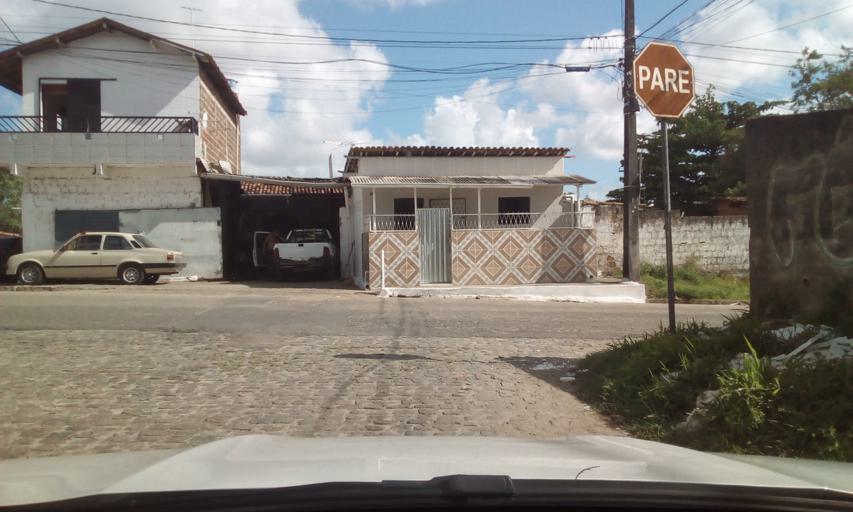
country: BR
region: Paraiba
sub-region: Joao Pessoa
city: Joao Pessoa
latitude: -7.1297
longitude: -34.8870
